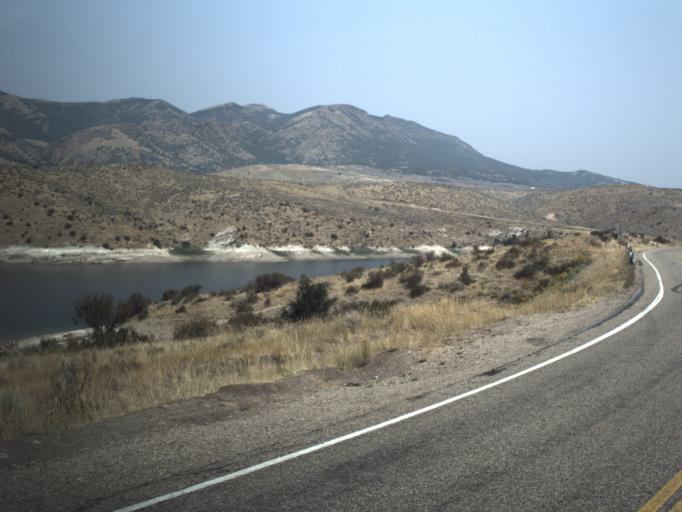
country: US
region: Utah
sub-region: Morgan County
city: Morgan
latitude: 40.9143
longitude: -111.5824
